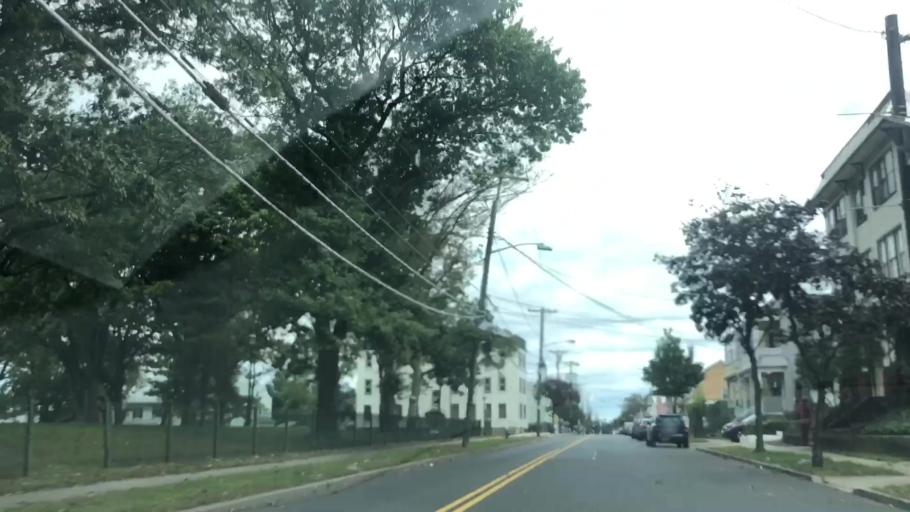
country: US
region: New Jersey
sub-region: Essex County
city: Irvington
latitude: 40.7197
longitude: -74.2260
